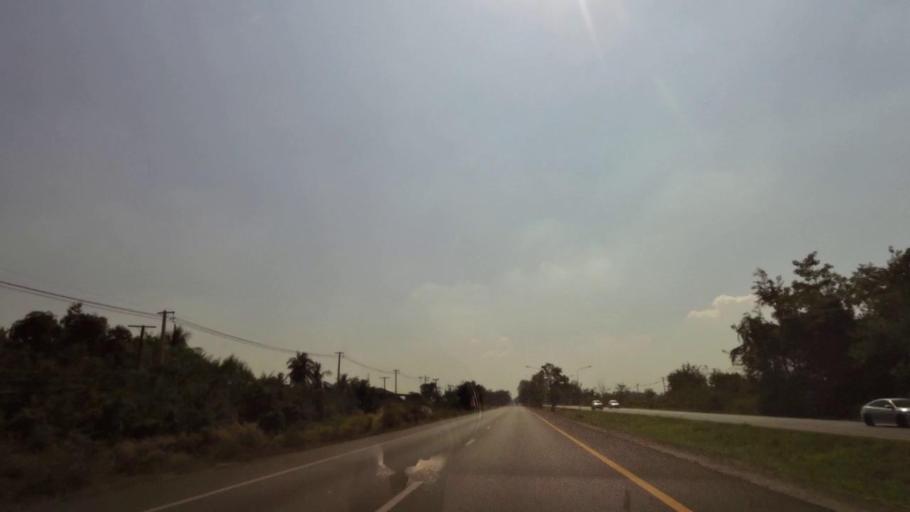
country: TH
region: Phichit
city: Bueng Na Rang
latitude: 16.2591
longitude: 100.1260
